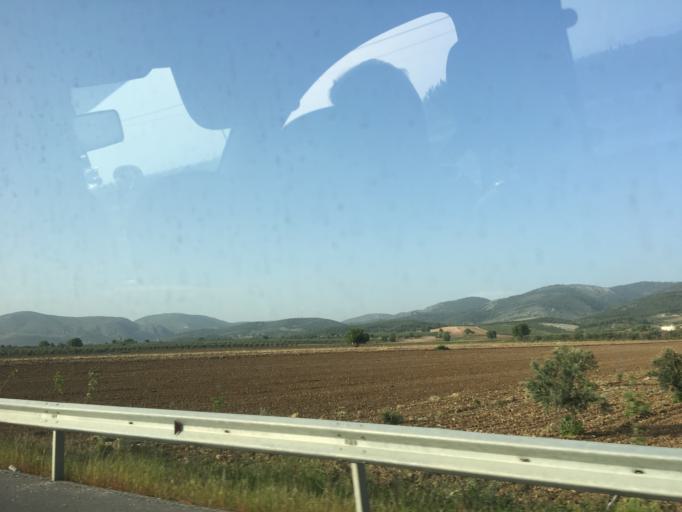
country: TR
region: Manisa
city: Golmarmara
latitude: 38.7922
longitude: 27.8999
